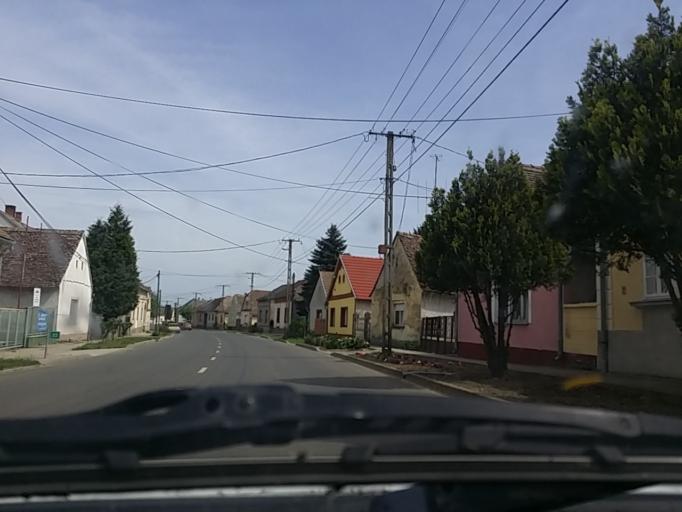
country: HU
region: Baranya
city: Vajszlo
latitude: 45.8587
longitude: 17.9851
